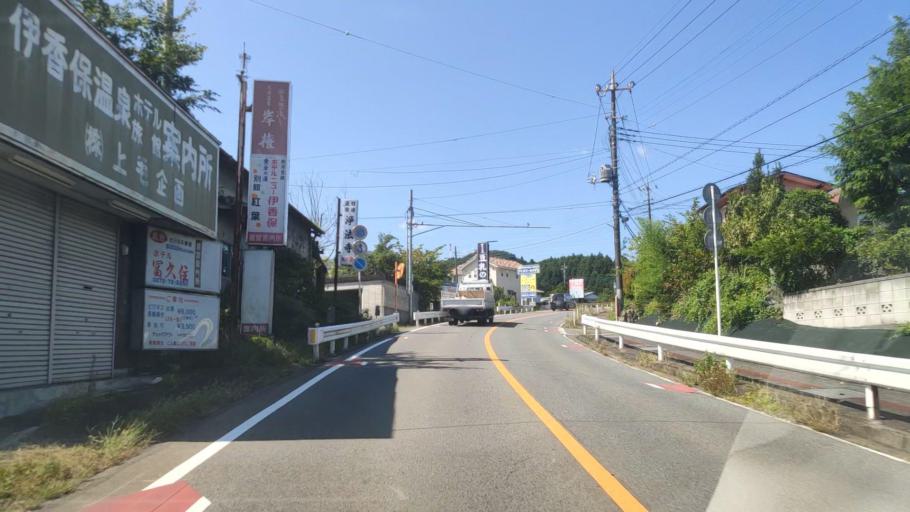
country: JP
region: Gunma
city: Shibukawa
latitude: 36.5009
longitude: 138.9856
